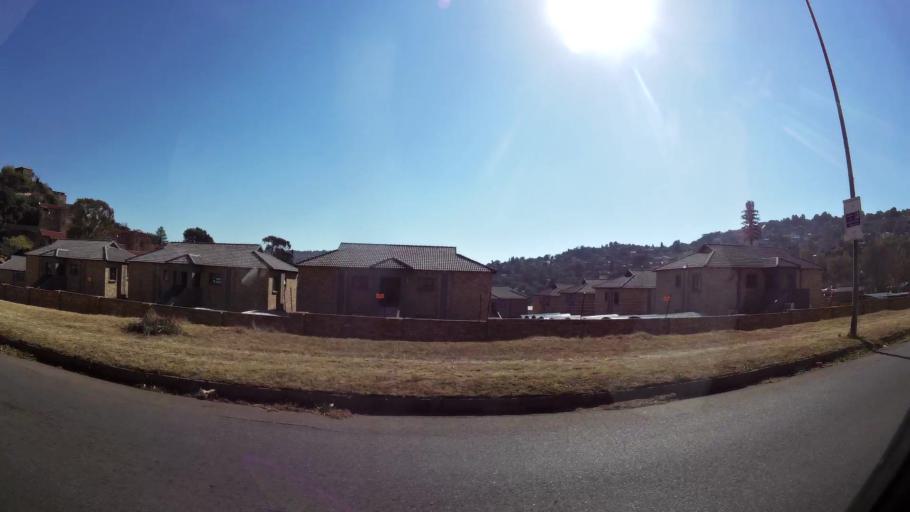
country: ZA
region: Gauteng
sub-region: City of Johannesburg Metropolitan Municipality
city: Roodepoort
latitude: -26.1248
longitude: 27.8742
